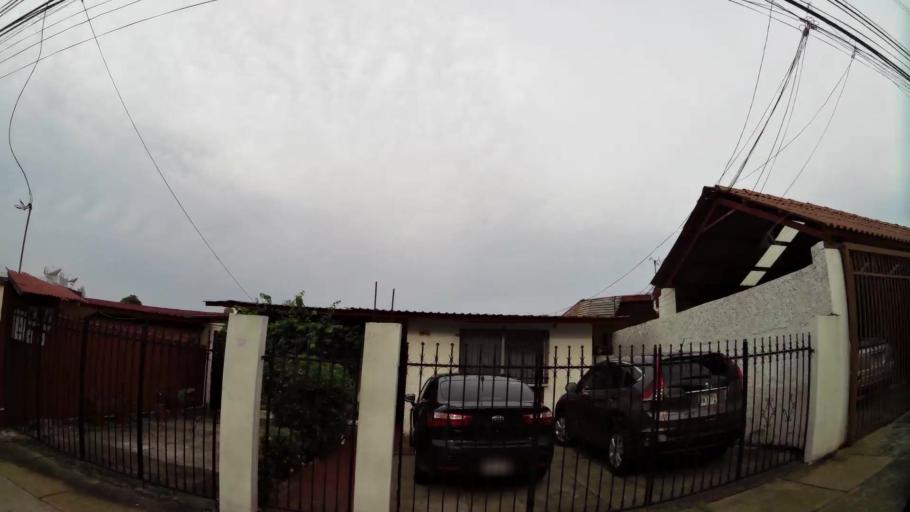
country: PA
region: Panama
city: Panama
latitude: 9.0098
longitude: -79.5097
